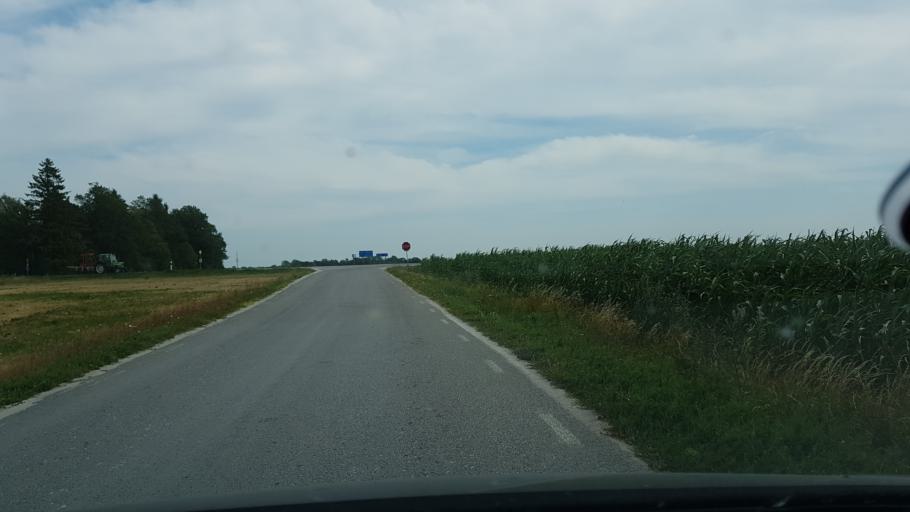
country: SE
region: Gotland
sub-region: Gotland
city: Visby
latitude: 57.7052
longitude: 18.5095
